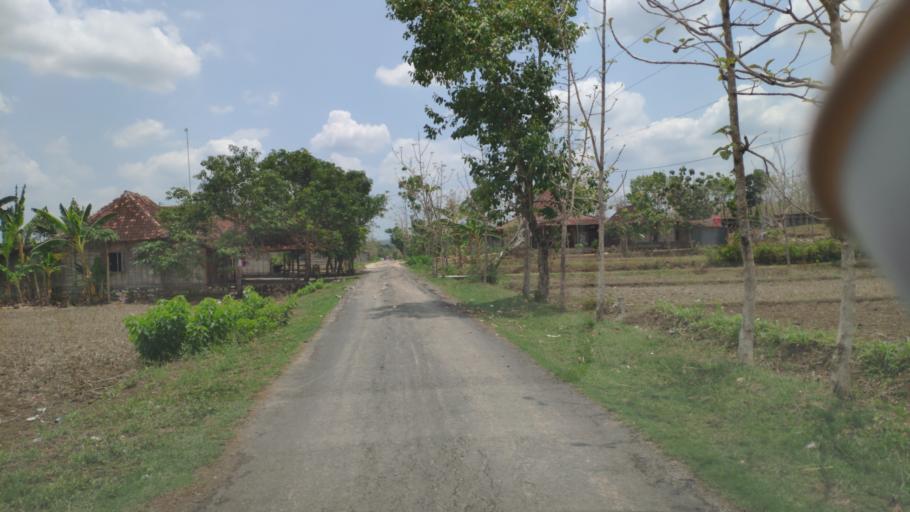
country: ID
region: Central Java
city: Gumiring
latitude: -7.0370
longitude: 111.3835
